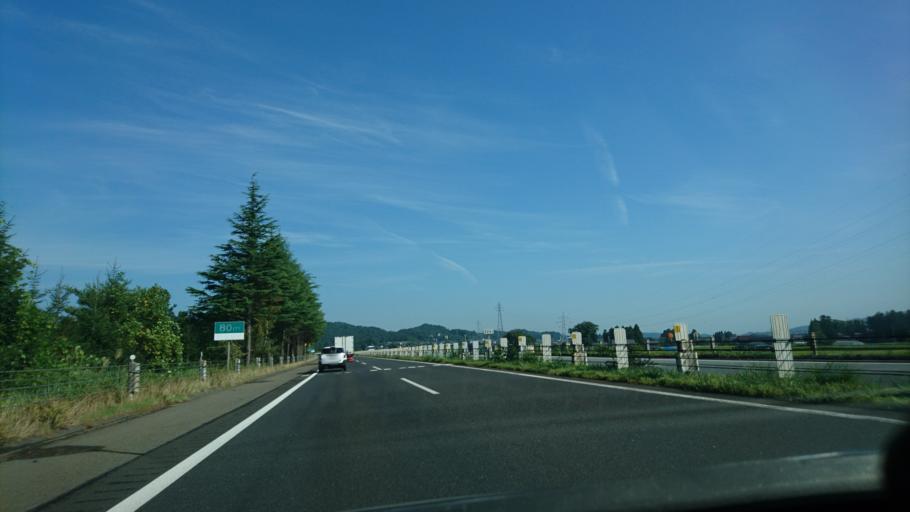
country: JP
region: Iwate
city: Ichinoseki
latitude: 38.9749
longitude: 141.1115
